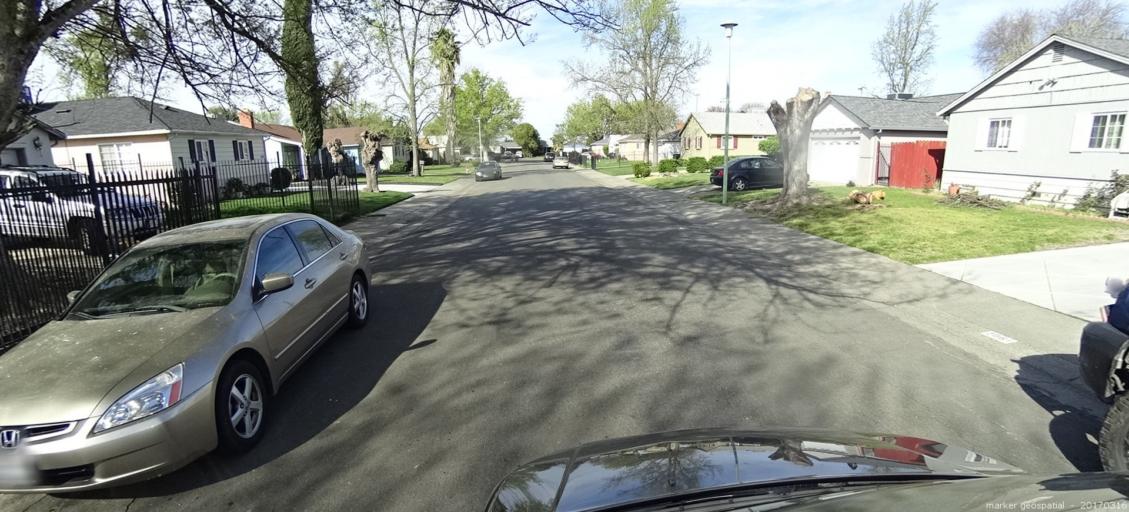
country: US
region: California
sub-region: Sacramento County
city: Parkway
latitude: 38.5098
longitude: -121.4902
